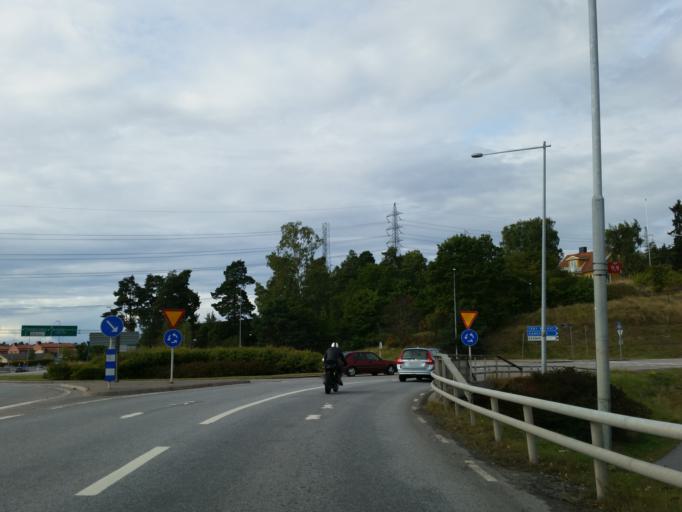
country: SE
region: Stockholm
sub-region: Sollentuna Kommun
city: Sollentuna
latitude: 59.4453
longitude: 17.9447
